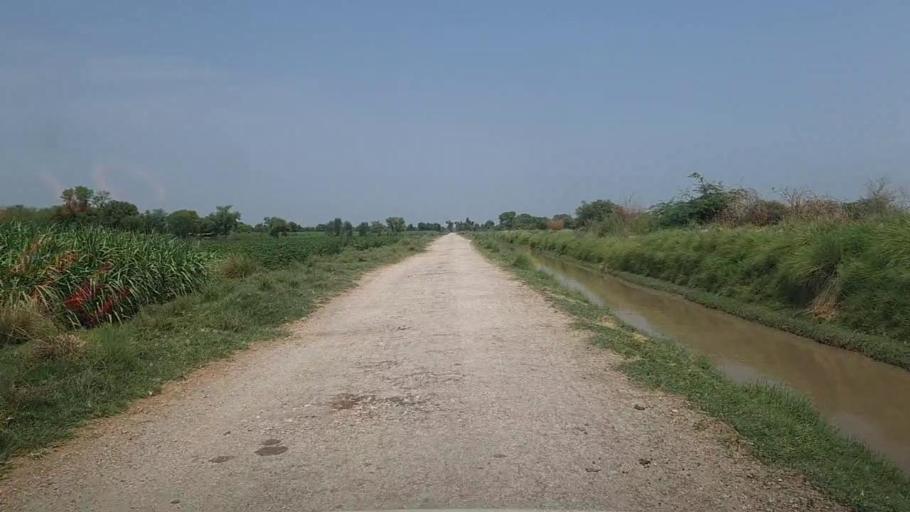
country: PK
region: Sindh
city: Karaundi
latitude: 26.8842
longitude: 68.3344
